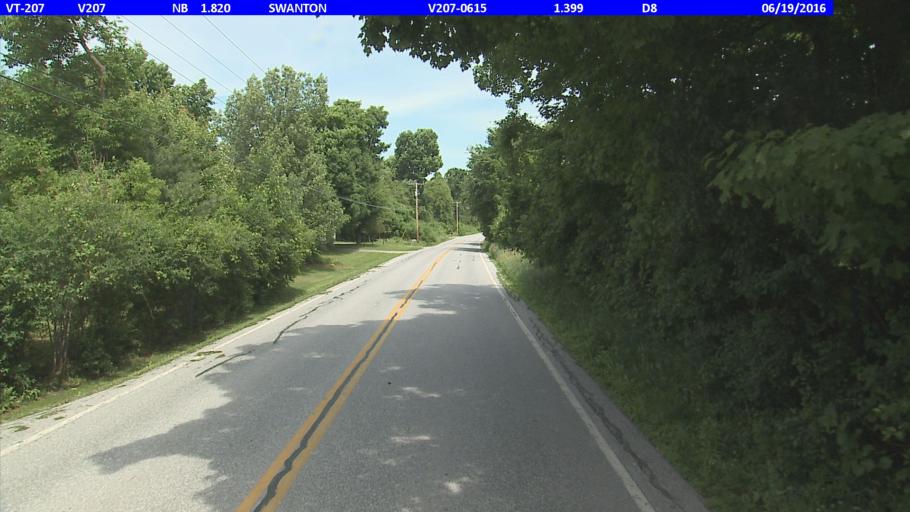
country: US
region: Vermont
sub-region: Franklin County
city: Saint Albans
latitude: 44.8652
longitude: -73.0752
